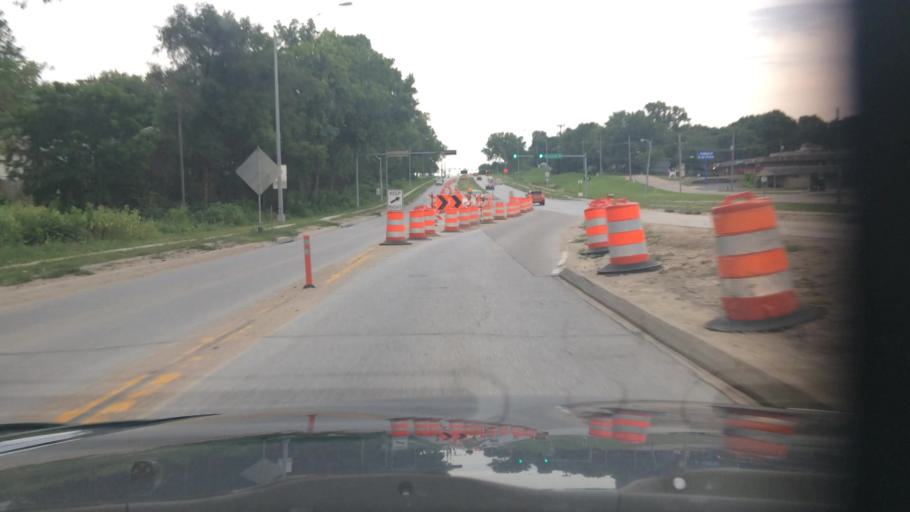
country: US
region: Nebraska
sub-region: Douglas County
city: Ralston
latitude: 41.1966
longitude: -96.0430
